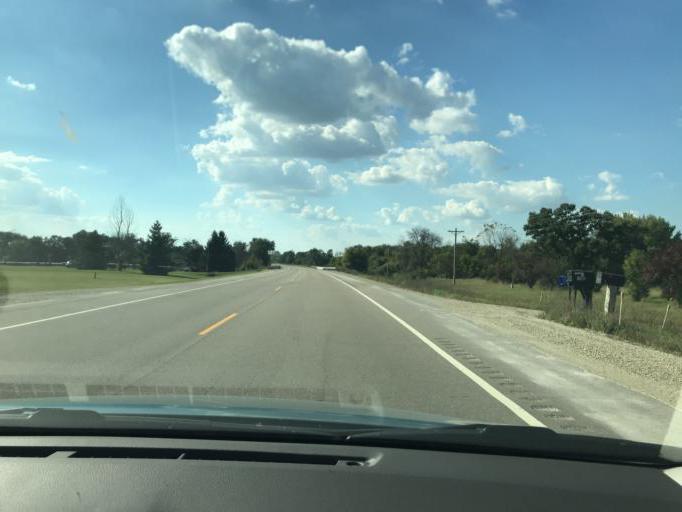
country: US
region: Wisconsin
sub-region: Green County
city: Brodhead
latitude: 42.5705
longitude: -89.3470
